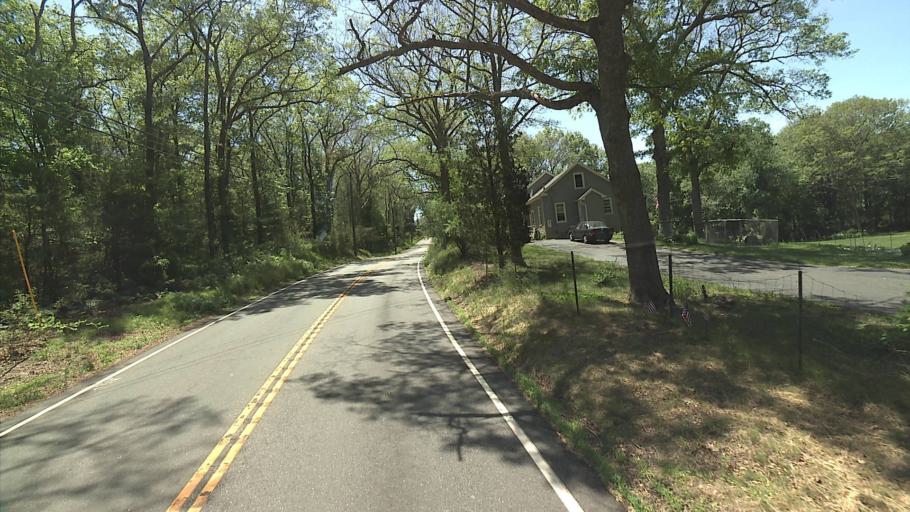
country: US
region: Rhode Island
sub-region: Washington County
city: Hopkinton
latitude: 41.5492
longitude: -71.8455
